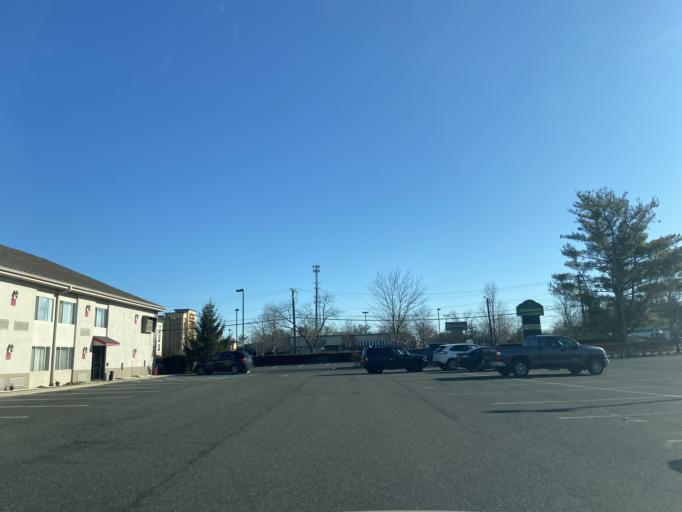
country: US
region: New Jersey
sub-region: Cumberland County
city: Vineland
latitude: 39.4887
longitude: -75.0682
